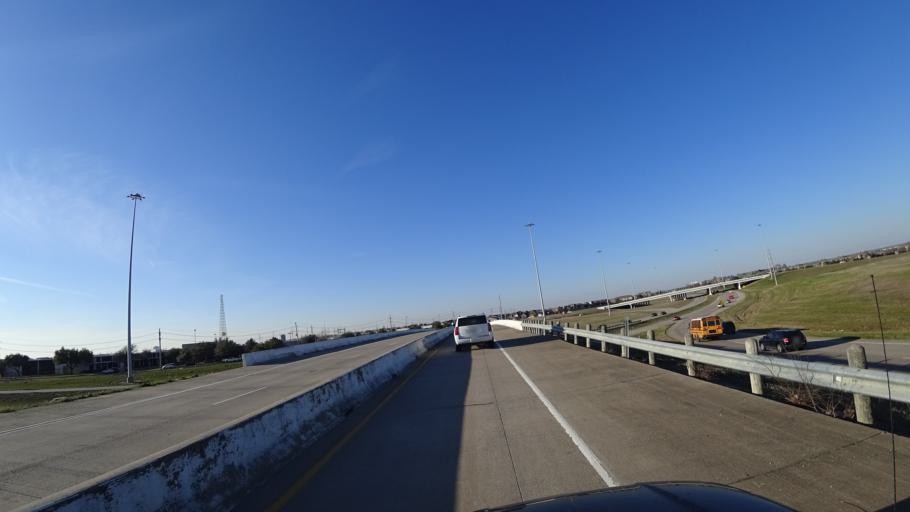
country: US
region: Texas
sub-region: Denton County
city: Lewisville
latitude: 33.0001
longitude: -96.9940
